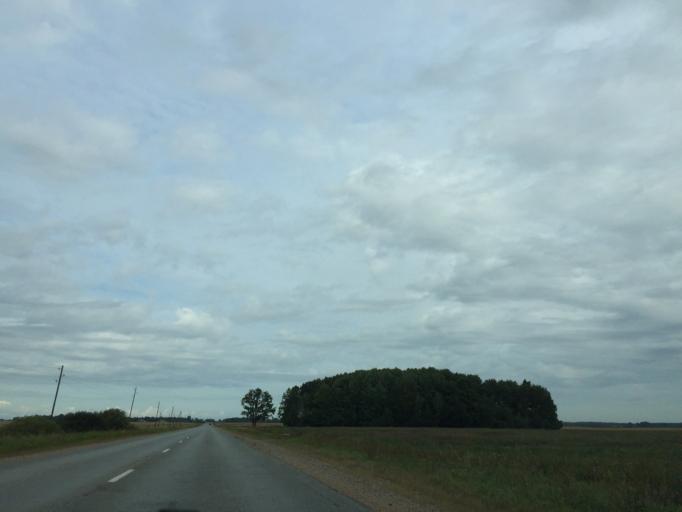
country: LV
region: Engure
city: Smarde
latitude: 56.7955
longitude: 23.3686
